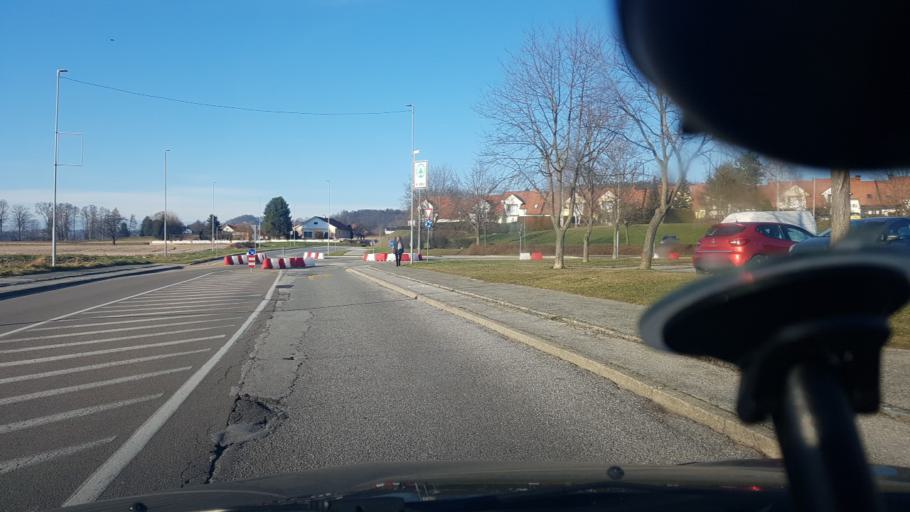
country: SI
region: Ptuj
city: Ptuj
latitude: 46.4298
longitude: 15.8675
